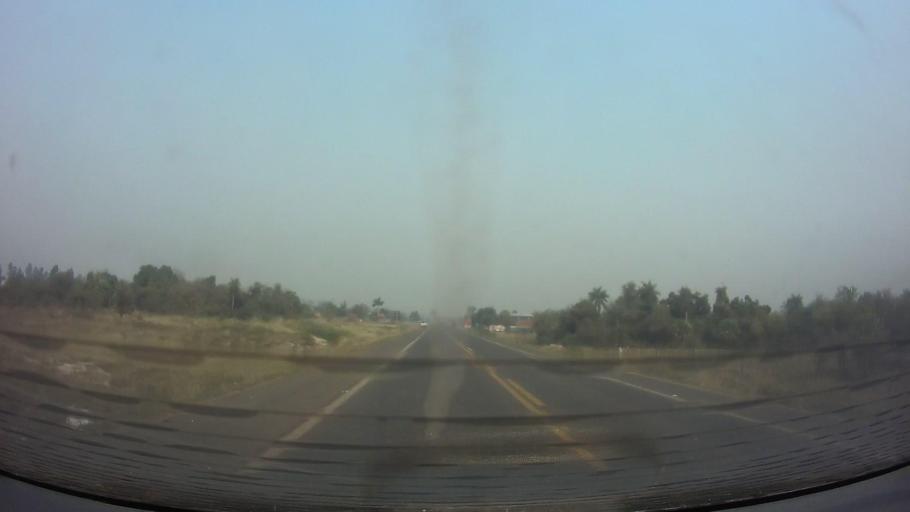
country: PY
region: Central
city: Limpio
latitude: -25.1637
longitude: -57.4905
